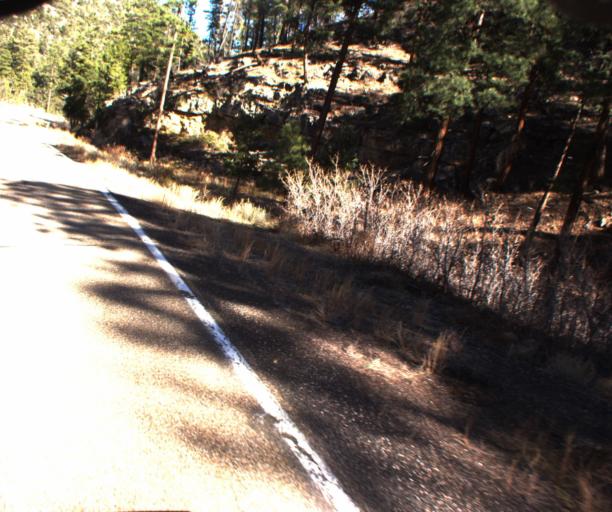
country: US
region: Arizona
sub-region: Coconino County
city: Fredonia
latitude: 36.7347
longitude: -112.1443
